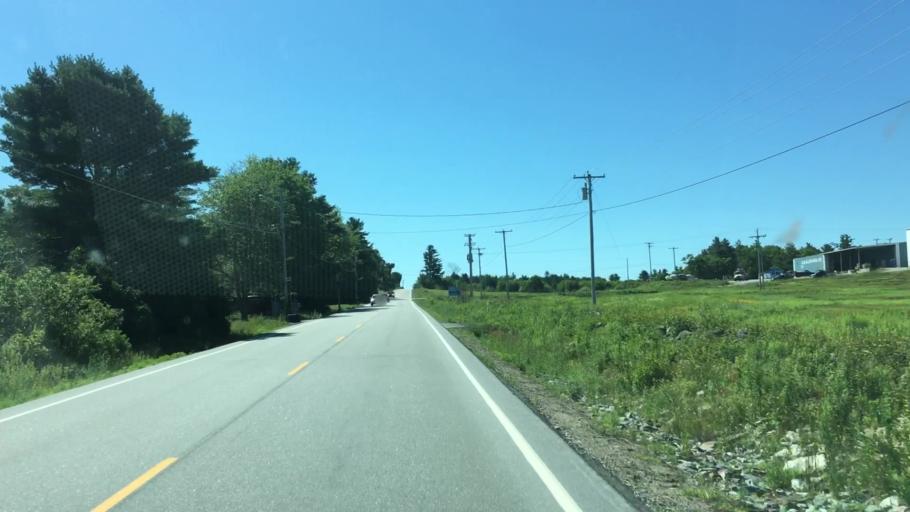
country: US
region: Maine
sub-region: Hancock County
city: Orland
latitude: 44.5511
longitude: -68.6922
